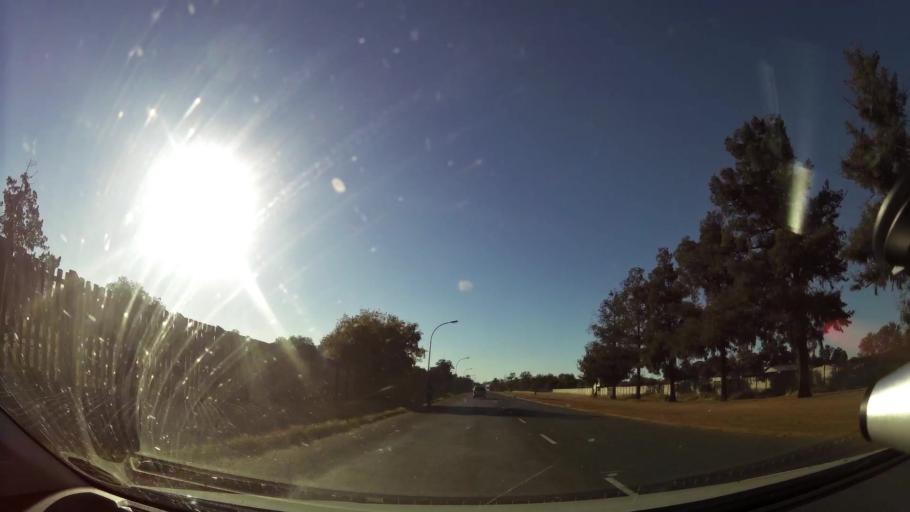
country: ZA
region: Northern Cape
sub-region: Frances Baard District Municipality
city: Kimberley
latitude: -28.7361
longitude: 24.7382
